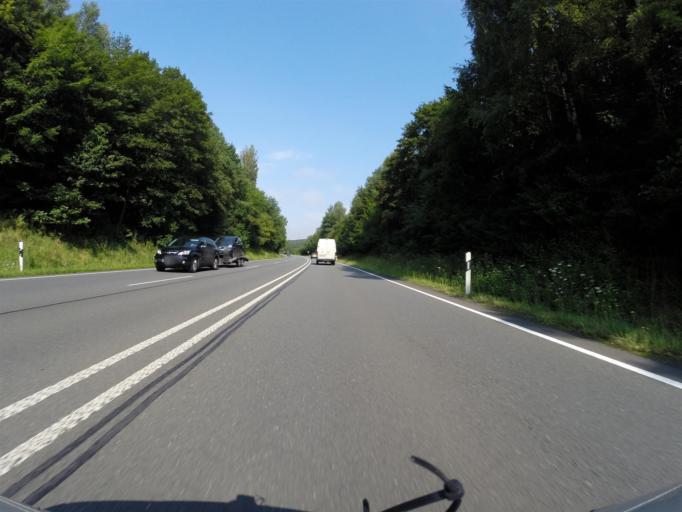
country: DE
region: Hesse
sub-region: Regierungsbezirk Kassel
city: Helsa
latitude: 51.2710
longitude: 9.6640
